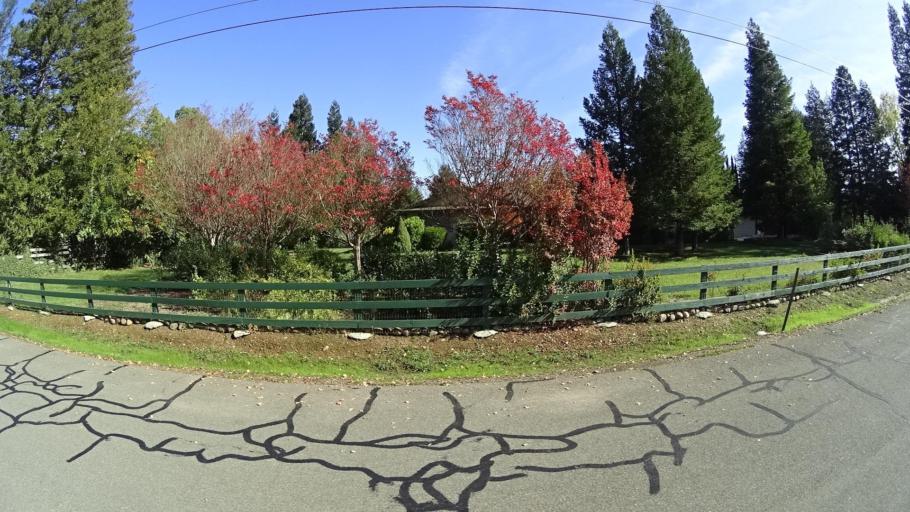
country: US
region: California
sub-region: Sacramento County
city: Elk Grove
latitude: 38.4360
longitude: -121.3579
